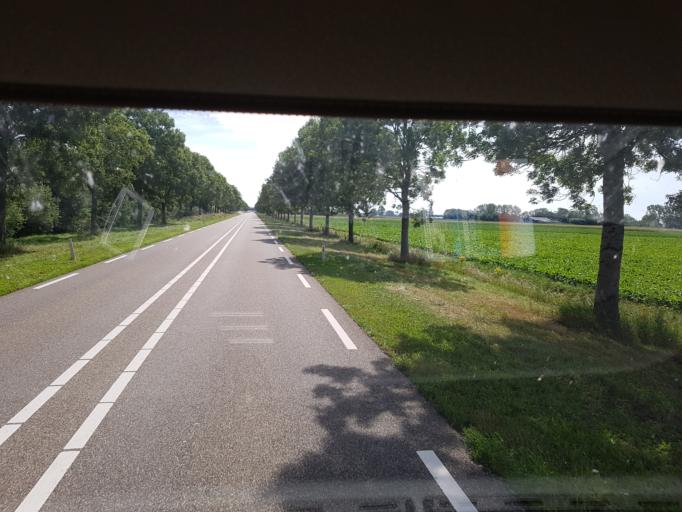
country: NL
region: North Brabant
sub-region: Gemeente Aalburg
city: Aalburg
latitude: 51.7714
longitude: 5.0637
